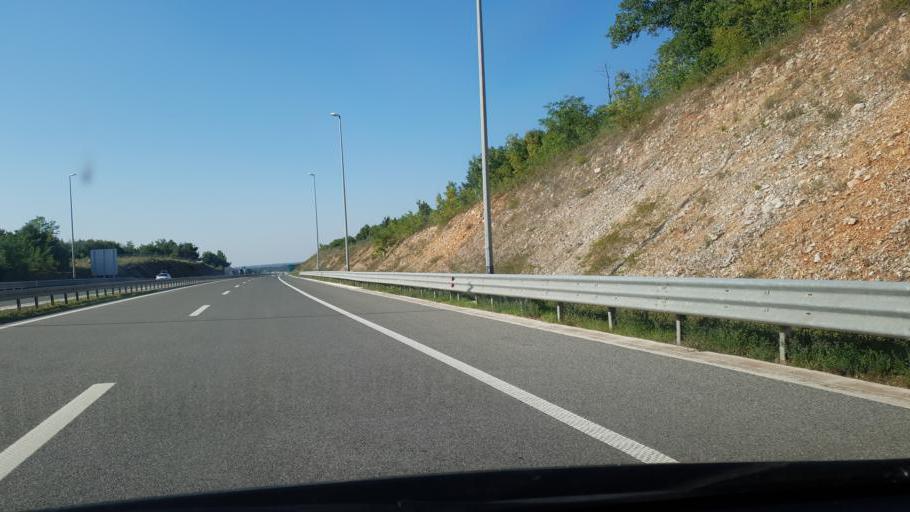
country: HR
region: Istarska
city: Vodnjan
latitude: 44.9553
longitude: 13.8721
